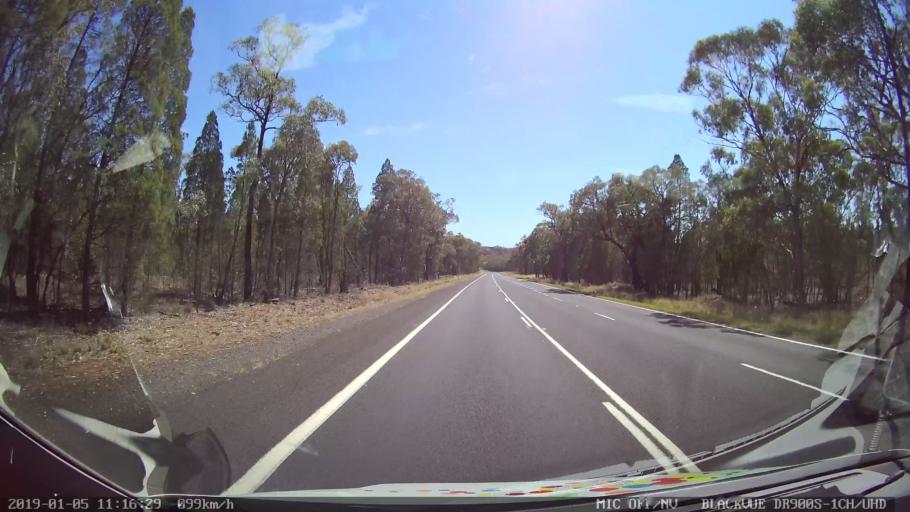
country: AU
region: New South Wales
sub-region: Warrumbungle Shire
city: Coonabarabran
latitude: -31.3381
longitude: 149.2986
